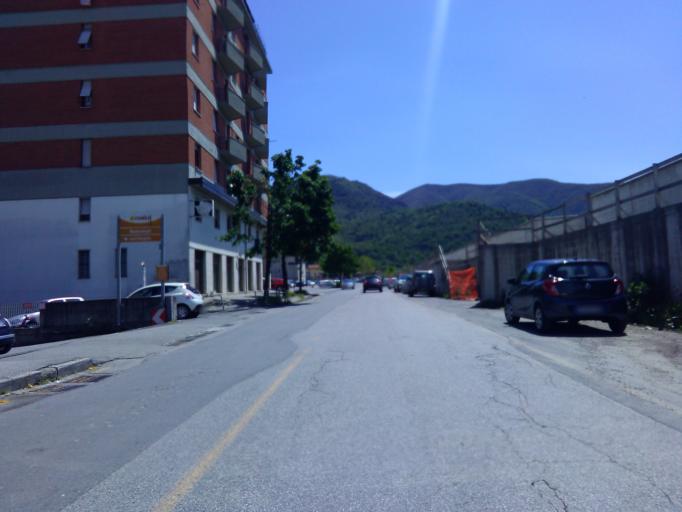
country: IT
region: Tuscany
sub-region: Provincia di Massa-Carrara
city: Aulla
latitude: 44.2103
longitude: 9.9672
